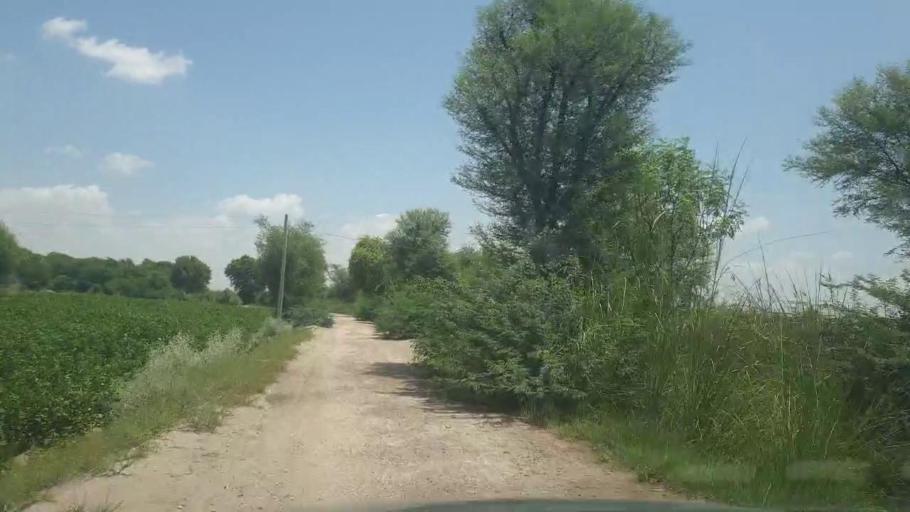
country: PK
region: Sindh
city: Kot Diji
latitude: 27.2629
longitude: 69.0247
